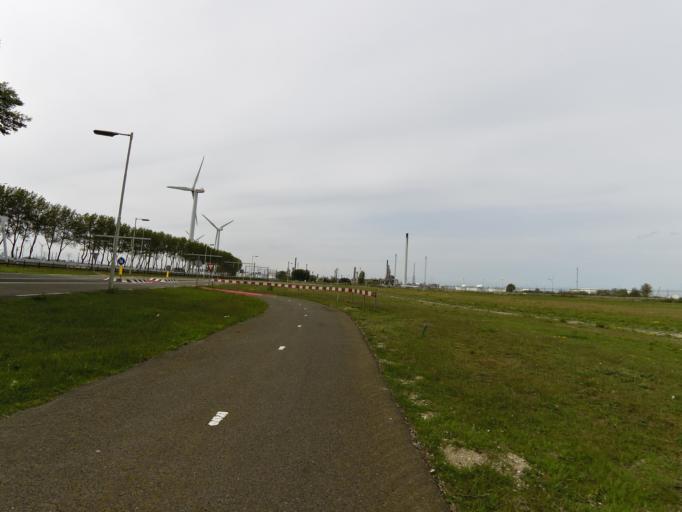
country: NL
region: South Holland
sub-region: Gemeente Brielle
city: Brielle
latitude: 51.9256
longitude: 4.1748
